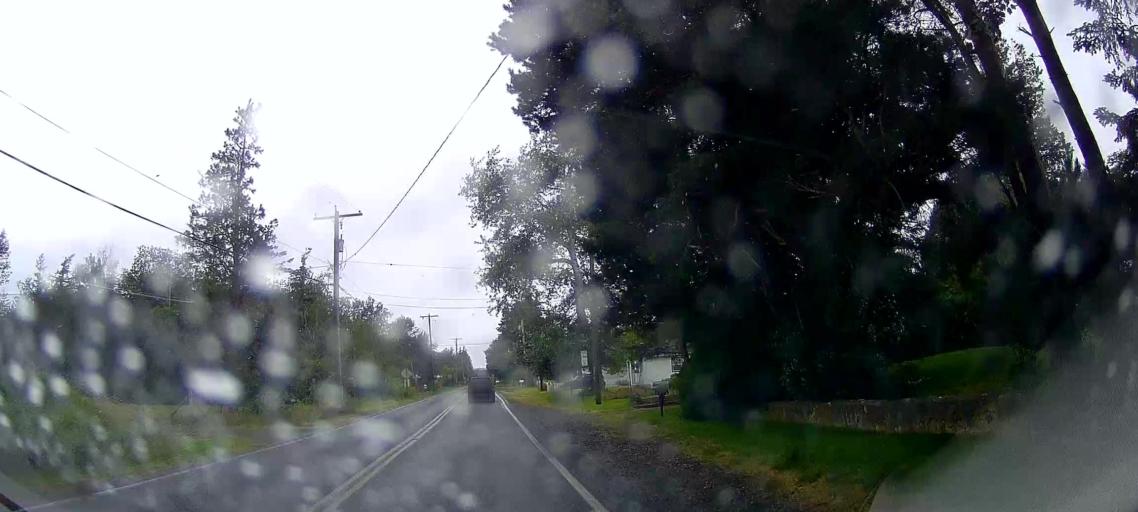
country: US
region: Washington
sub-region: Whatcom County
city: Marietta-Alderwood
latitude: 48.7834
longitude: -122.5521
